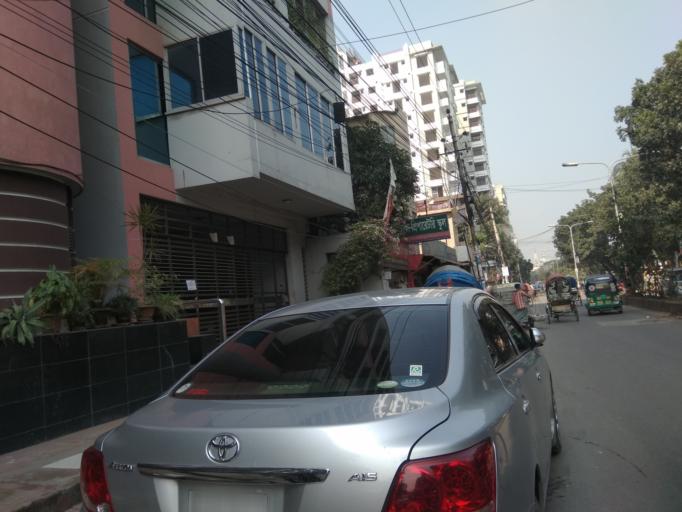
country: BD
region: Dhaka
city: Azimpur
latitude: 23.7639
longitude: 90.3656
